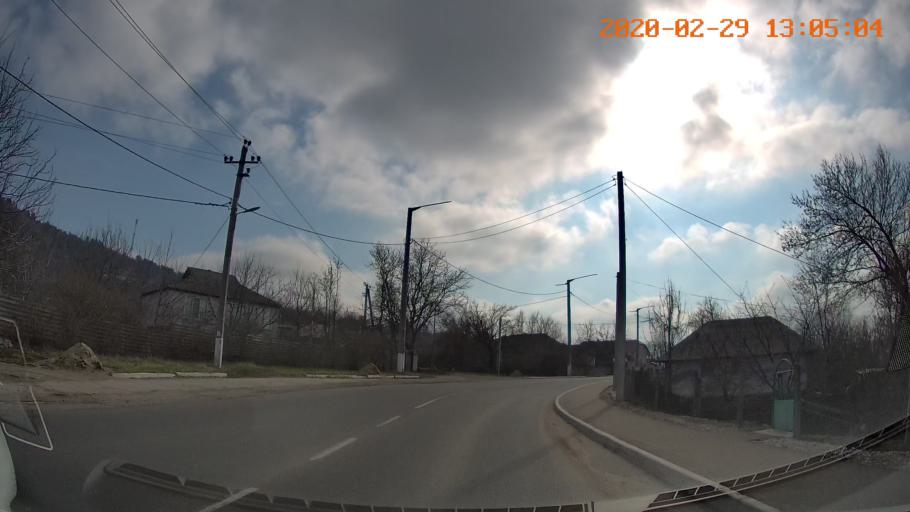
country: MD
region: Telenesti
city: Camenca
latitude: 48.0232
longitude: 28.7082
